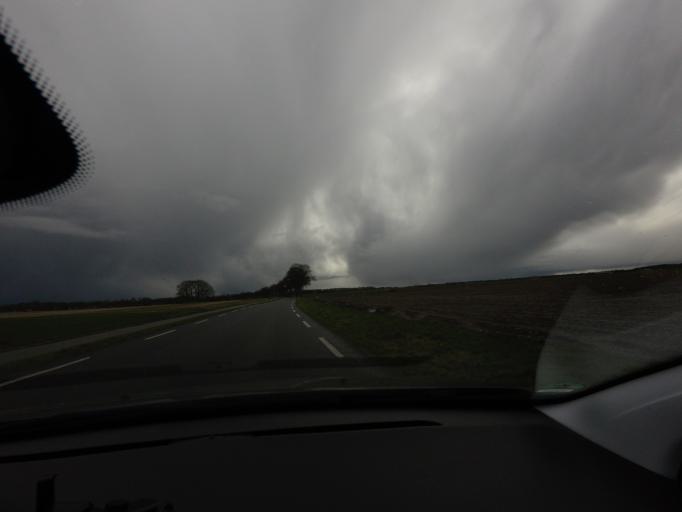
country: NL
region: Drenthe
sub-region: Gemeente Borger-Odoorn
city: Borger
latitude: 52.9386
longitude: 6.7888
